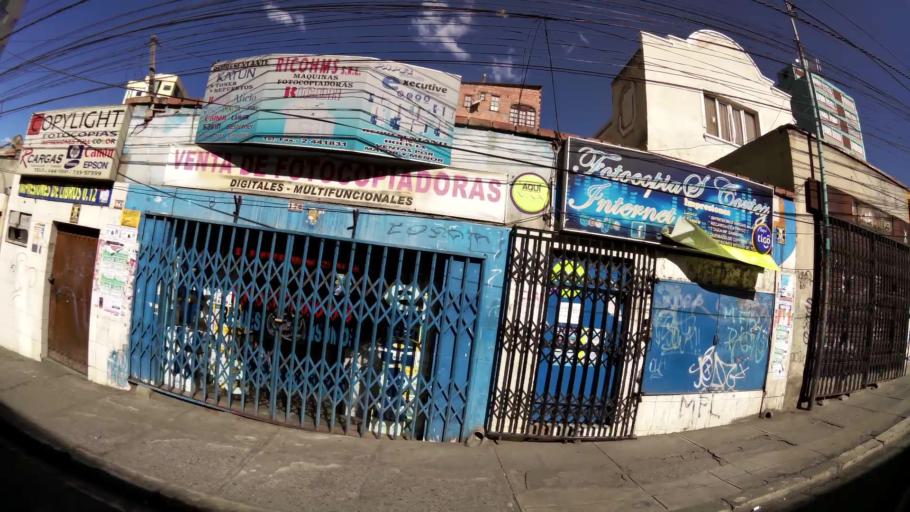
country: BO
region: La Paz
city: La Paz
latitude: -16.5049
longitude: -68.1290
